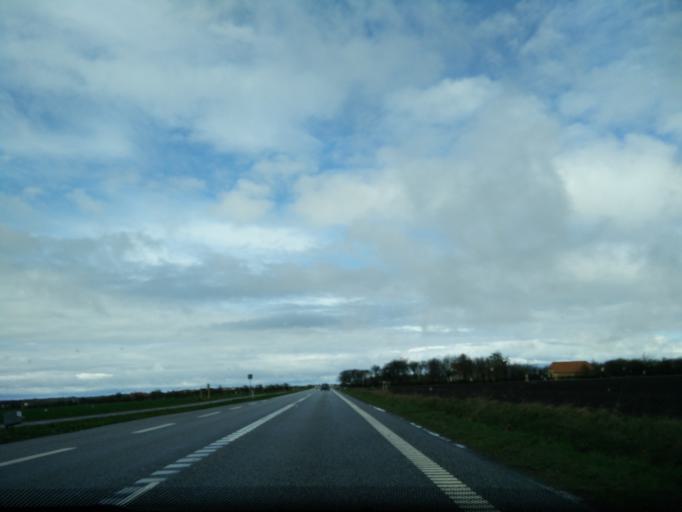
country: DK
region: Central Jutland
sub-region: Ringkobing-Skjern Kommune
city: Ringkobing
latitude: 56.1134
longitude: 8.1818
